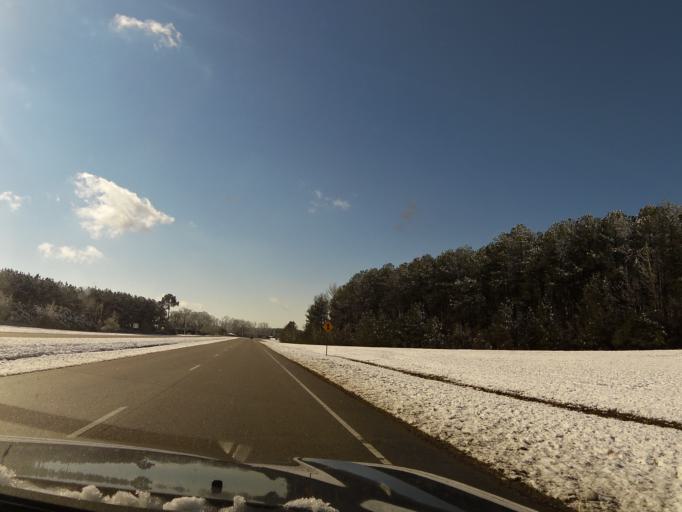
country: US
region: North Carolina
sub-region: Wilson County
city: Elm City
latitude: 35.7657
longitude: -77.8583
